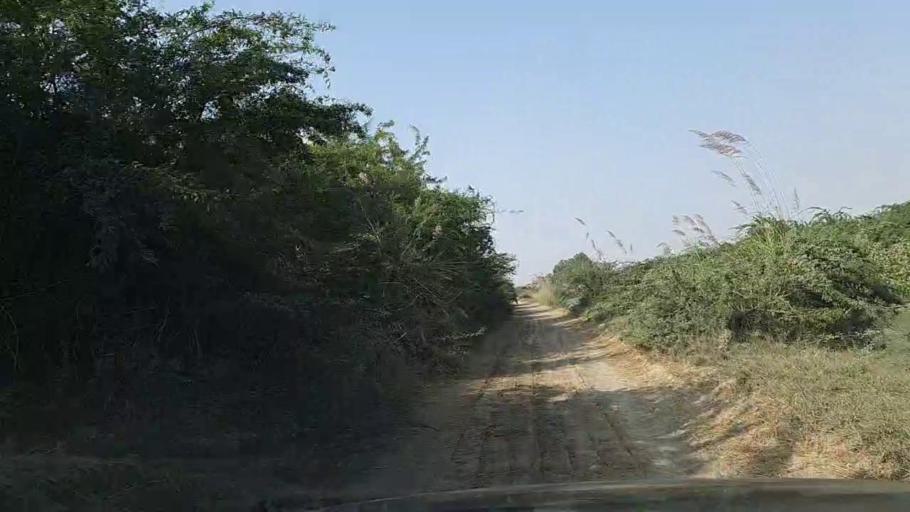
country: PK
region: Sindh
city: Gharo
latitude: 24.7279
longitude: 67.7060
